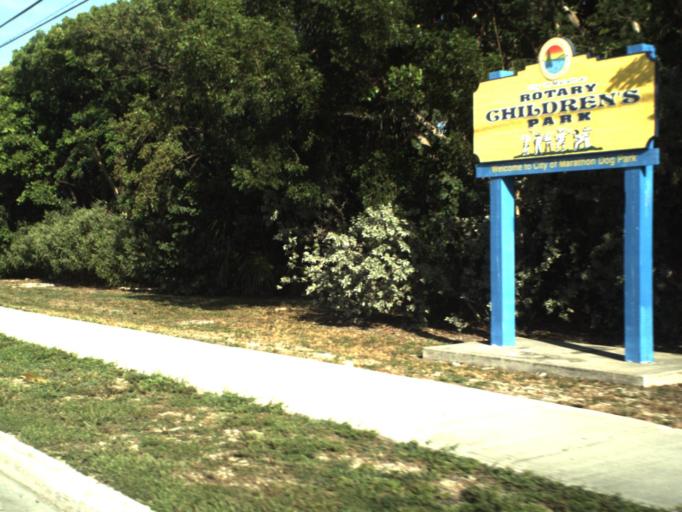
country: US
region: Florida
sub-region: Monroe County
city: Marathon
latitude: 24.7212
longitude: -81.0594
